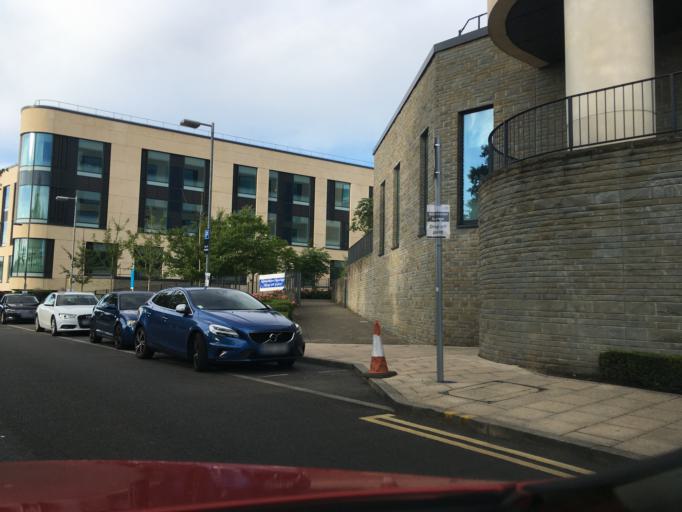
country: GB
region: England
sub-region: Bristol
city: Bristol
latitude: 51.4954
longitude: -2.5901
